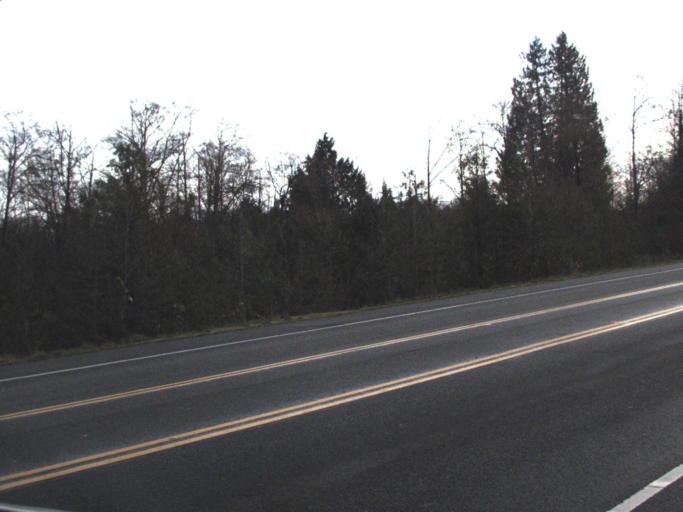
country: US
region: Washington
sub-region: Snohomish County
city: Cathcart
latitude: 47.8766
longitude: -122.1098
